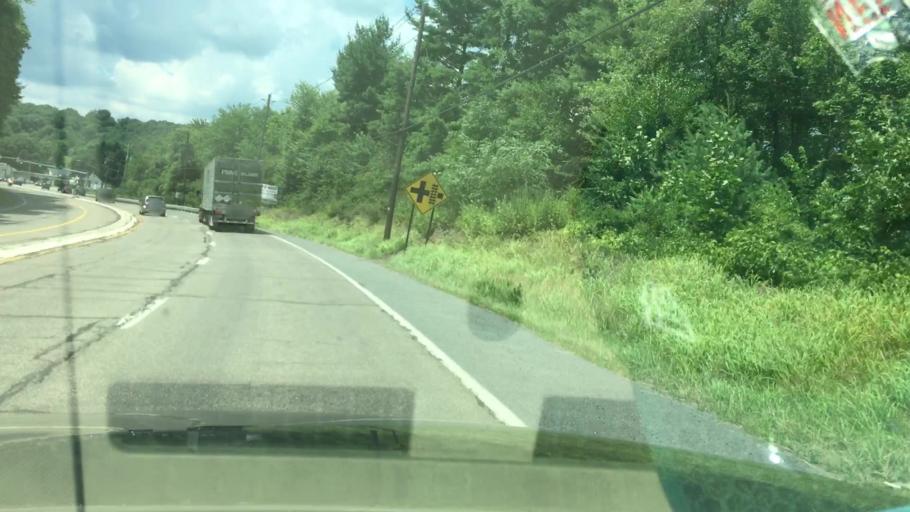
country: US
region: Pennsylvania
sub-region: Schuylkill County
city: Minersville
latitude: 40.6809
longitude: -76.2499
